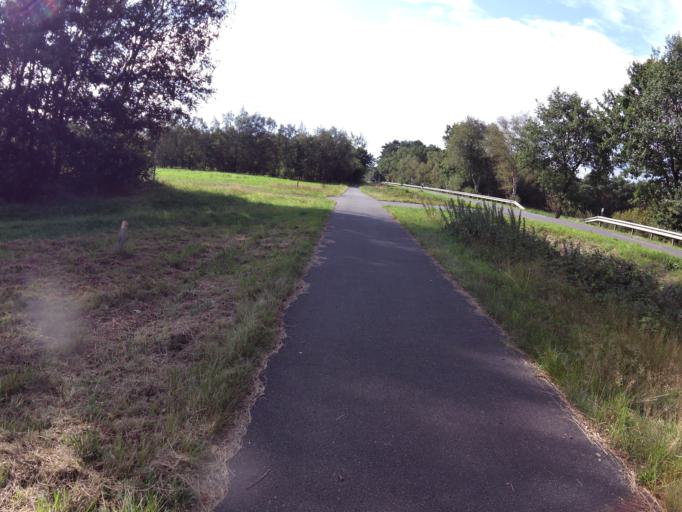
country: DE
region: Lower Saxony
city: Bremervorde
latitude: 53.4641
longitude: 9.1412
